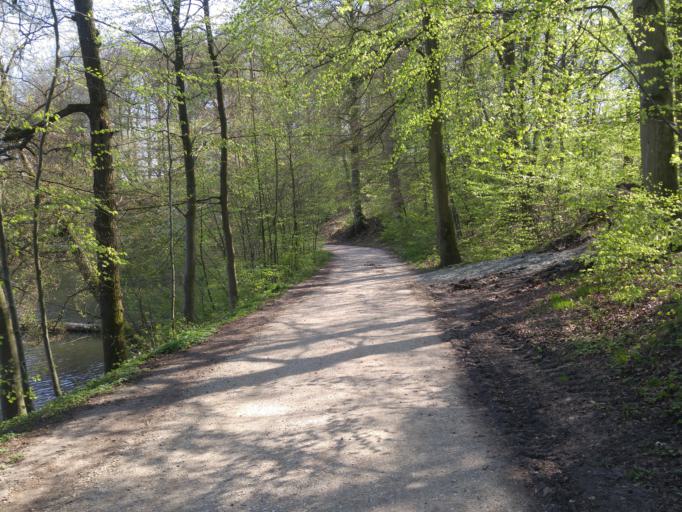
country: DK
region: South Denmark
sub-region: Kolding Kommune
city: Kolding
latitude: 55.4992
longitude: 9.4878
